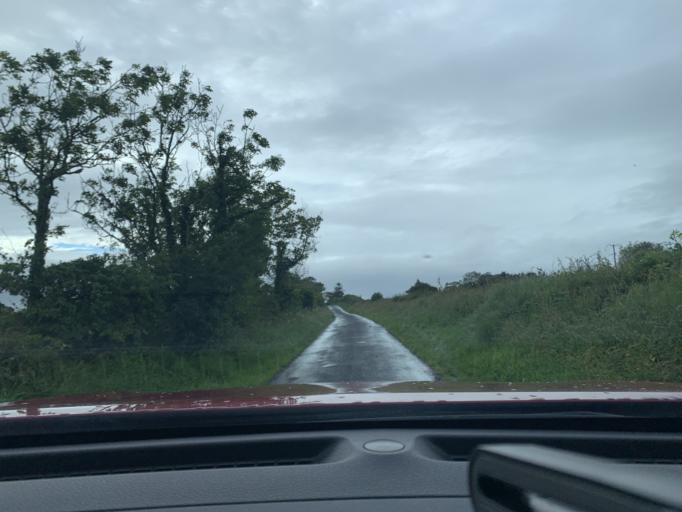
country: IE
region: Connaught
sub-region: Sligo
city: Strandhill
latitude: 54.3651
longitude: -8.5561
